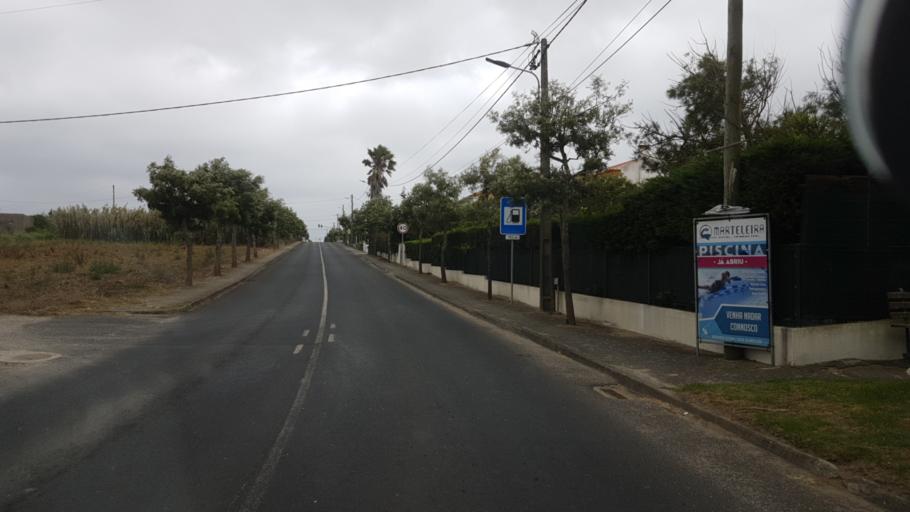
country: PT
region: Lisbon
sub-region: Lourinha
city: Lourinha
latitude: 39.2152
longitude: -9.3217
